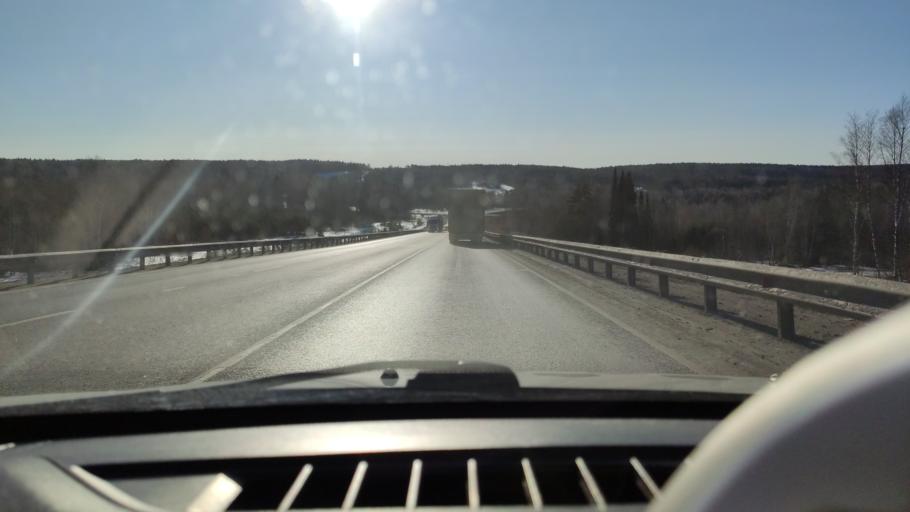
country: RU
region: Perm
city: Suksun
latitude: 57.0924
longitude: 57.3765
